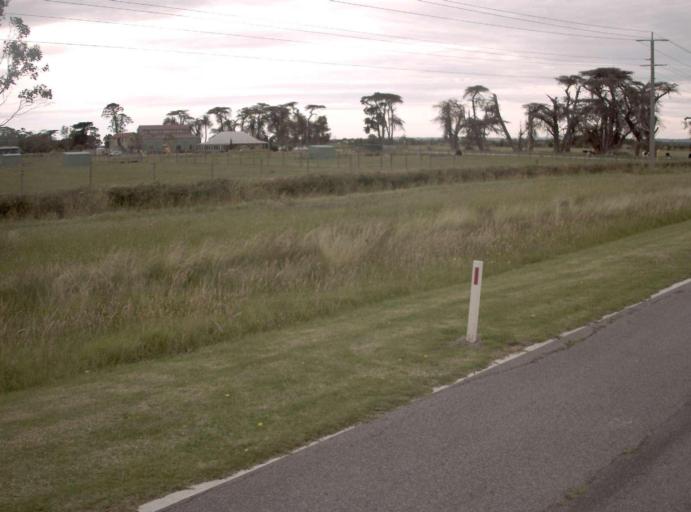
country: AU
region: Victoria
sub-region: Cardinia
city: Koo-Wee-Rup
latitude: -38.2412
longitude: 145.5270
